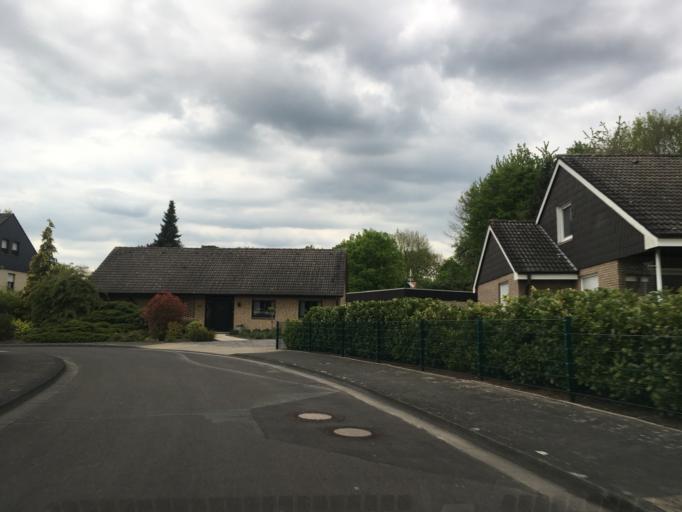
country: DE
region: North Rhine-Westphalia
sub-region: Regierungsbezirk Munster
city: Steinfurt
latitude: 52.1514
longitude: 7.3552
